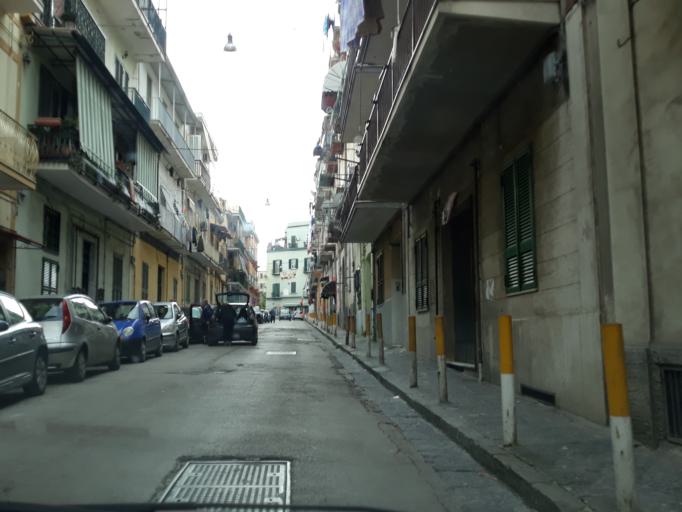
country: IT
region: Campania
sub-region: Provincia di Napoli
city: Mugnano di Napoli
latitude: 40.8868
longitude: 14.2294
